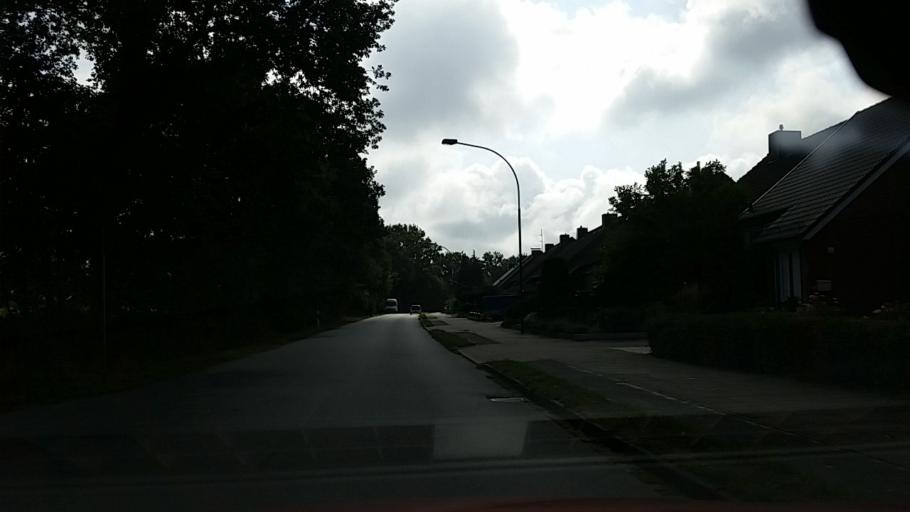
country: DE
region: Schleswig-Holstein
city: Rellingen
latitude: 53.6262
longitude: 9.7846
